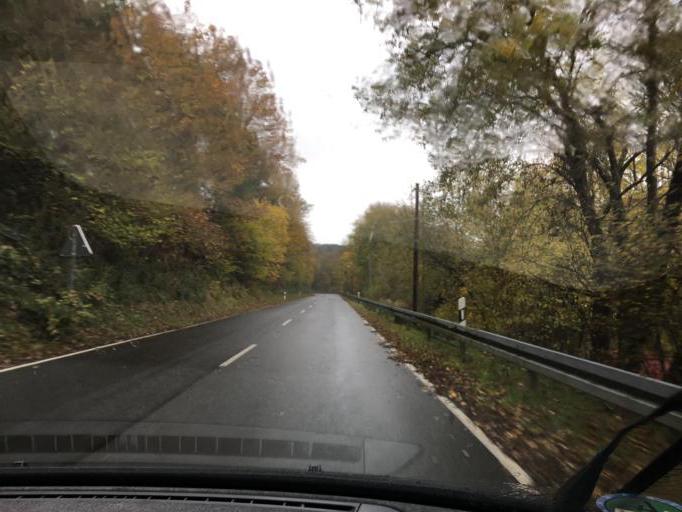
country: DE
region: North Rhine-Westphalia
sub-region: Regierungsbezirk Koln
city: Simmerath
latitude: 50.6260
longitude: 6.3815
